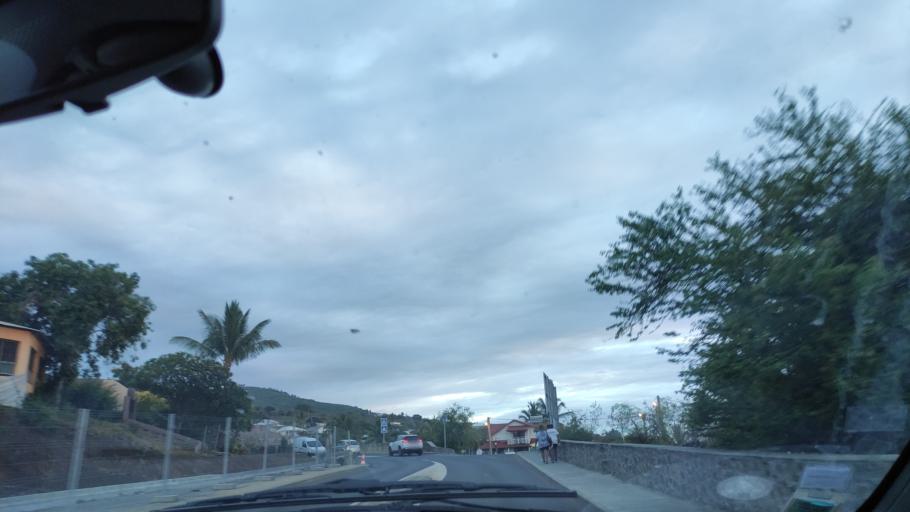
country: RE
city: Piton Saint-Leu
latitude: -21.2102
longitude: 55.2988
